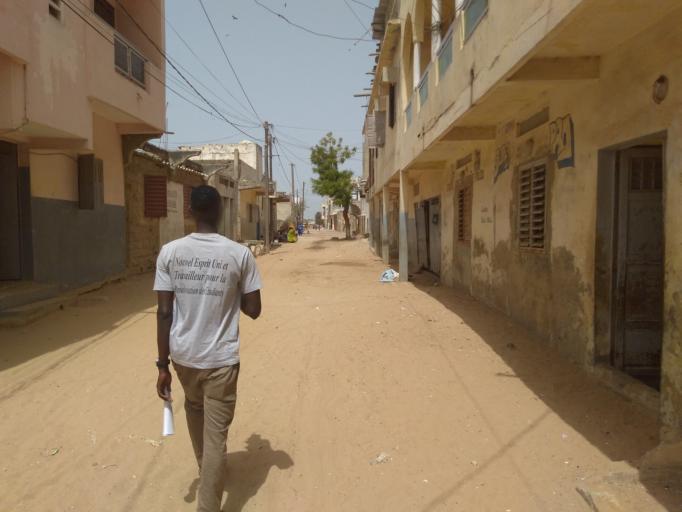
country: SN
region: Dakar
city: Pikine
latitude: 14.7911
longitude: -17.3371
